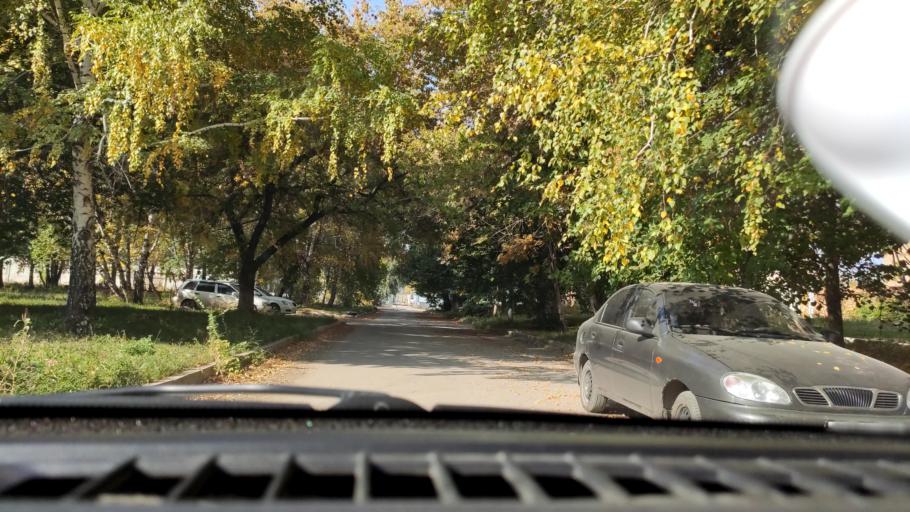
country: RU
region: Samara
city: Smyshlyayevka
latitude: 53.1898
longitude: 50.2754
